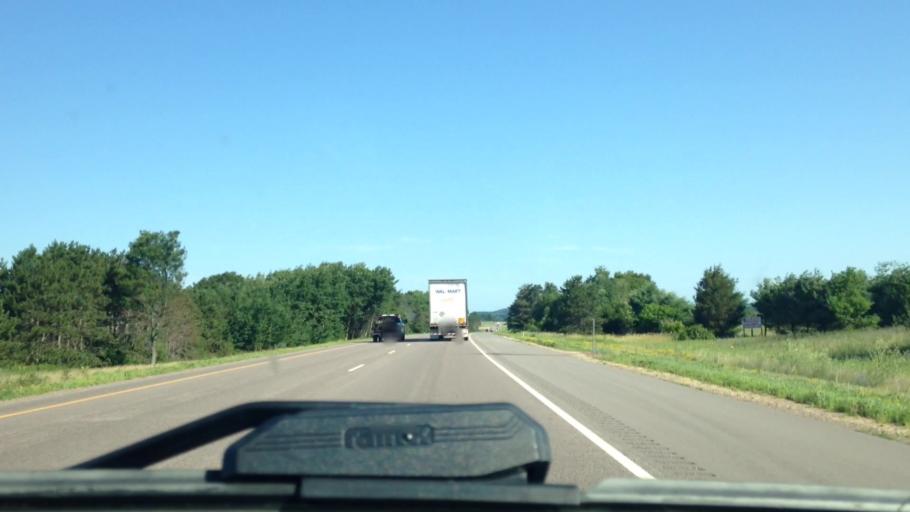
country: US
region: Wisconsin
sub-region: Trempealeau County
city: Osseo
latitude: 44.5230
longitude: -91.1459
